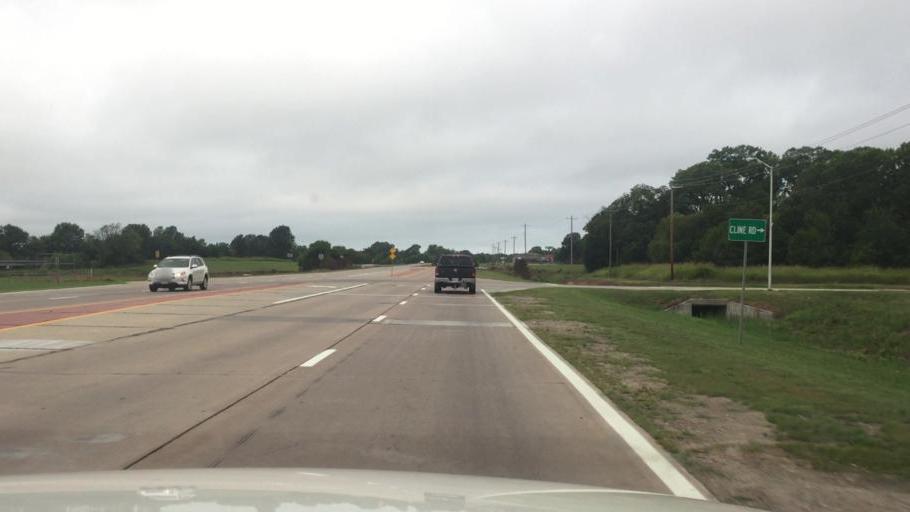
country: US
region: Kansas
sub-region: Montgomery County
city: Coffeyville
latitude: 37.0334
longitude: -95.6468
